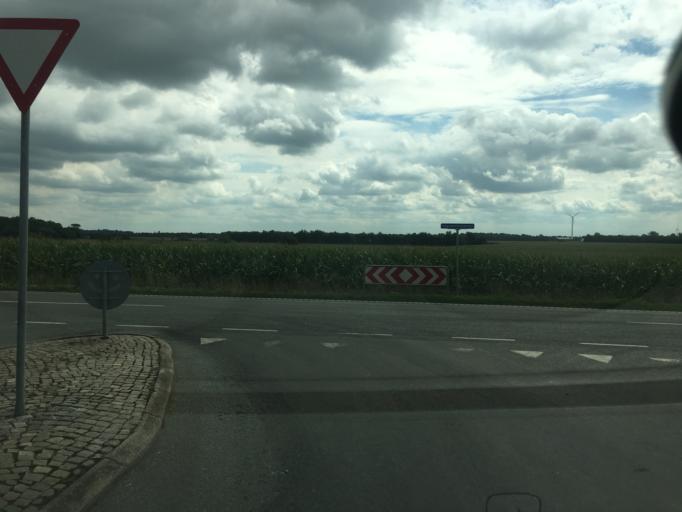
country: DK
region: South Denmark
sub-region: Tonder Kommune
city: Toftlund
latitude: 55.1155
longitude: 9.0397
